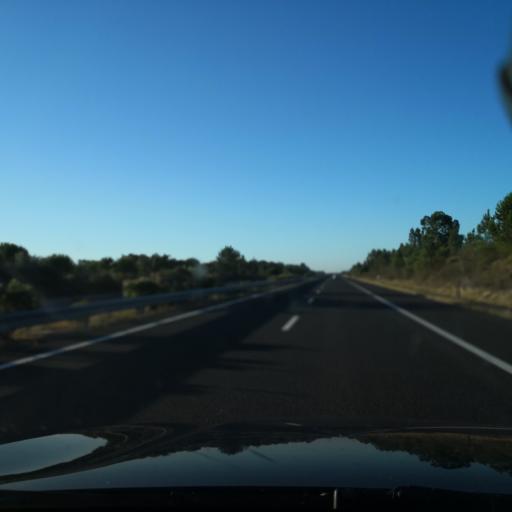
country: PT
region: Santarem
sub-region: Benavente
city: Poceirao
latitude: 38.8071
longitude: -8.7029
